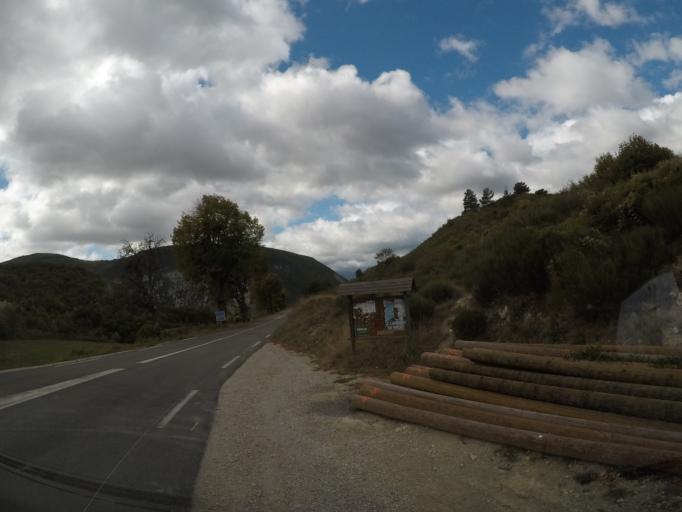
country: FR
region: Provence-Alpes-Cote d'Azur
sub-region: Departement du Vaucluse
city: Sault
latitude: 44.1821
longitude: 5.5099
